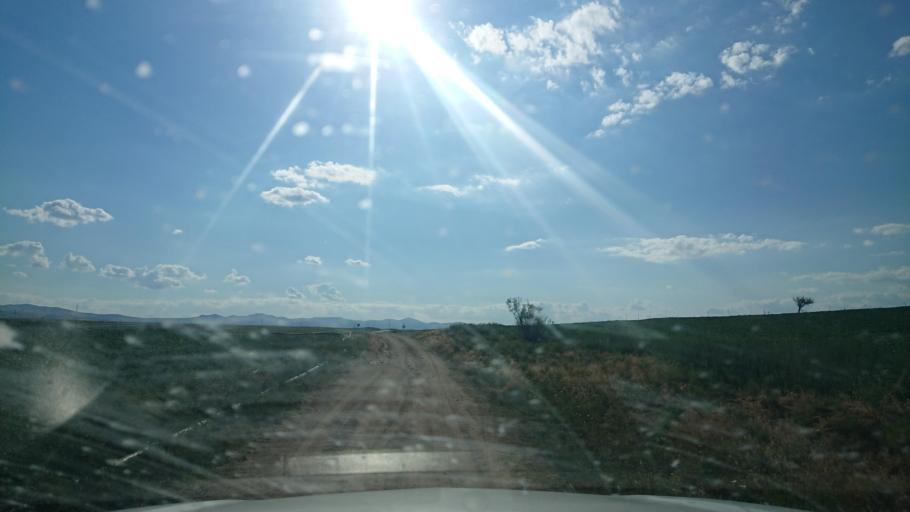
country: TR
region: Aksaray
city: Sariyahsi
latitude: 39.0197
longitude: 33.8898
